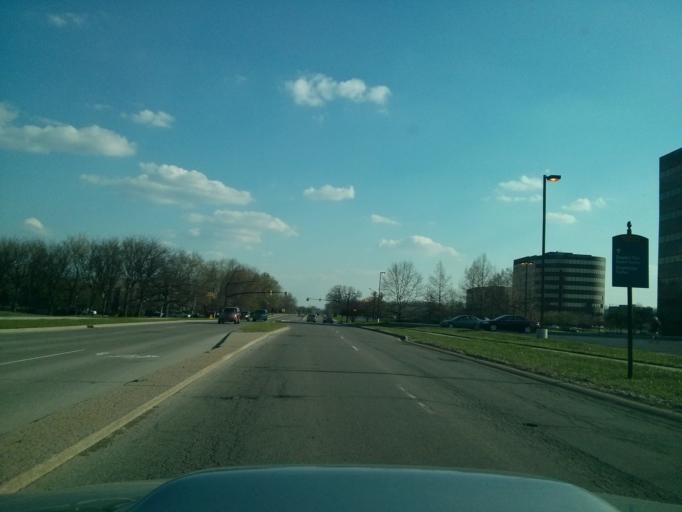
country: US
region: Indiana
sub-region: Hamilton County
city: Carmel
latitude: 39.9578
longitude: -86.1552
